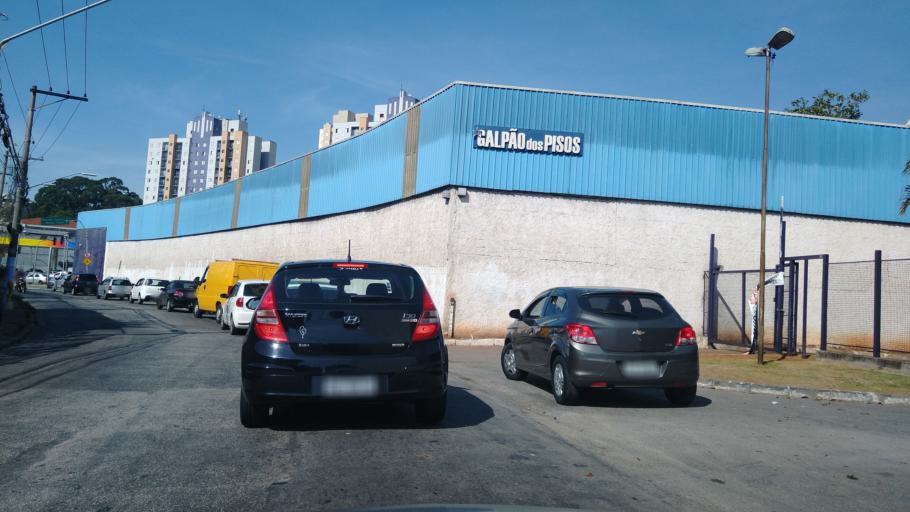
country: BR
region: Sao Paulo
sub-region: Sao Paulo
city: Sao Paulo
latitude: -23.4678
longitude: -46.6689
